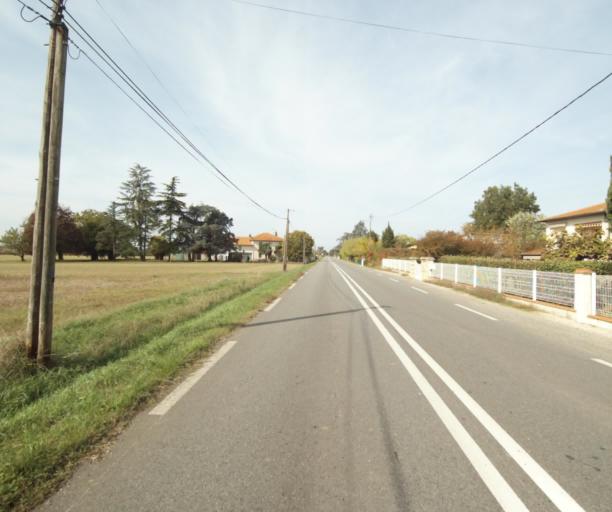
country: FR
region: Midi-Pyrenees
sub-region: Departement du Tarn-et-Garonne
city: Orgueil
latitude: 43.9203
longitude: 1.3958
